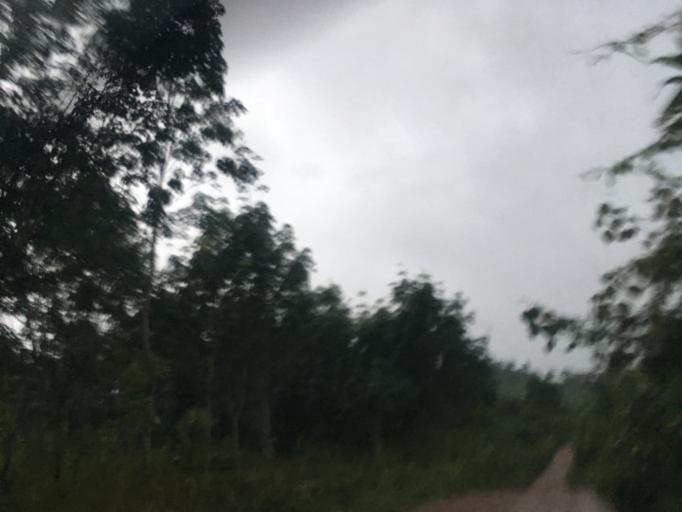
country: LA
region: Oudomxai
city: Muang La
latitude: 21.2504
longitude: 101.9322
